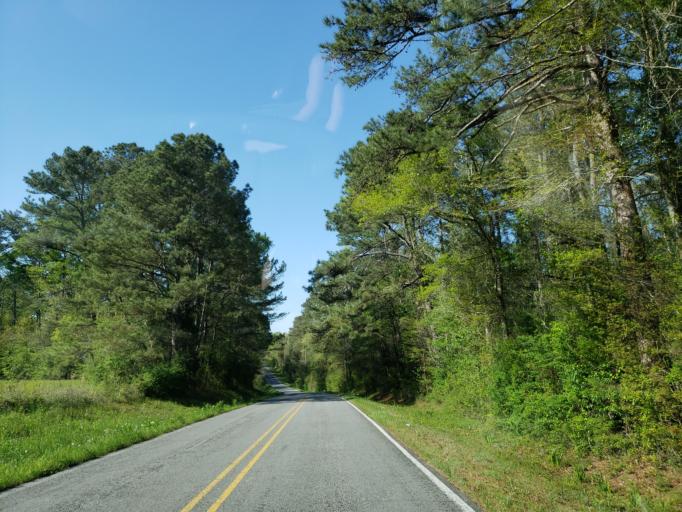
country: US
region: Mississippi
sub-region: Forrest County
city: Rawls Springs
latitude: 31.5221
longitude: -89.3589
